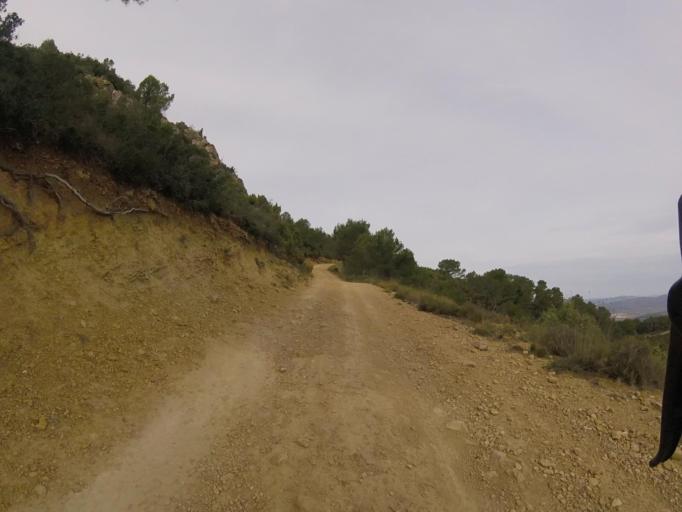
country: ES
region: Valencia
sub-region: Provincia de Castello
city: Benicassim
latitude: 40.0869
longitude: 0.0379
